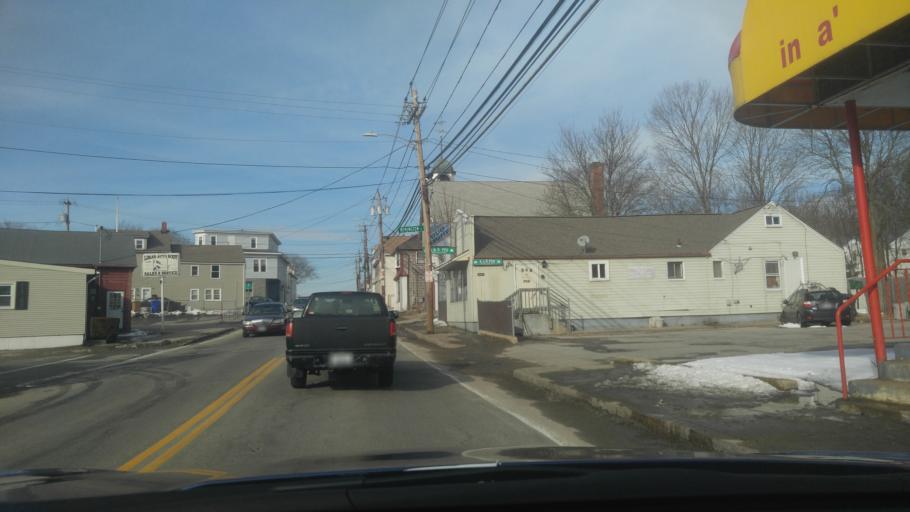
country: US
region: Rhode Island
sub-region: Kent County
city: West Warwick
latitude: 41.6866
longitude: -71.5229
